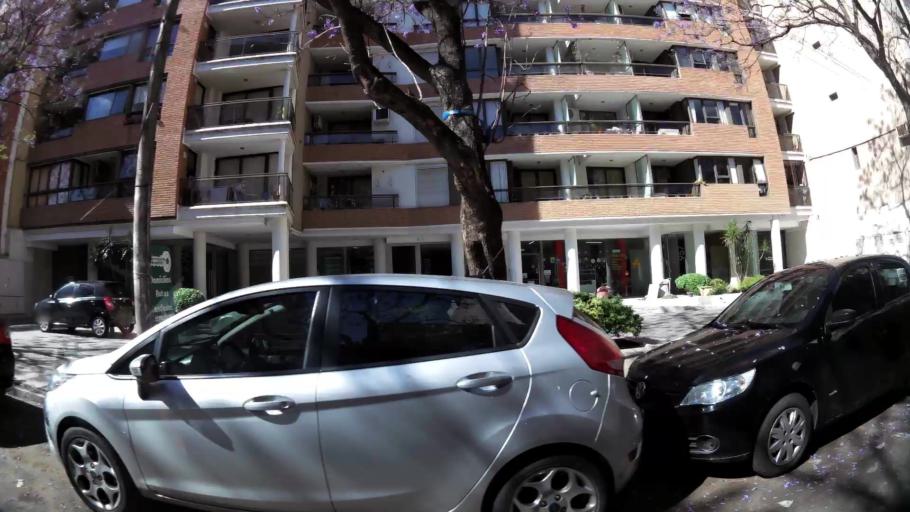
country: AR
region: Santa Fe
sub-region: Departamento de Rosario
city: Rosario
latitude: -32.9542
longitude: -60.6380
